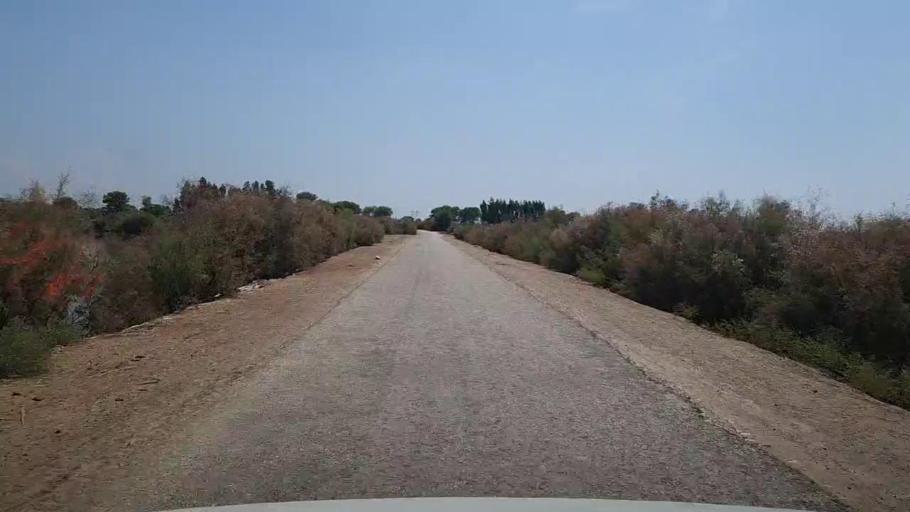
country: PK
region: Sindh
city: Kandhkot
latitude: 28.2943
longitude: 69.3516
